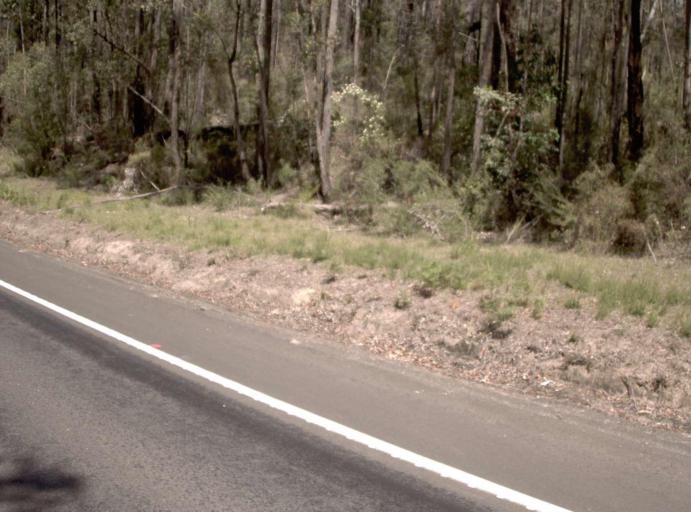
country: AU
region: New South Wales
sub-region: Bombala
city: Bombala
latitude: -37.5646
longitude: 149.0549
